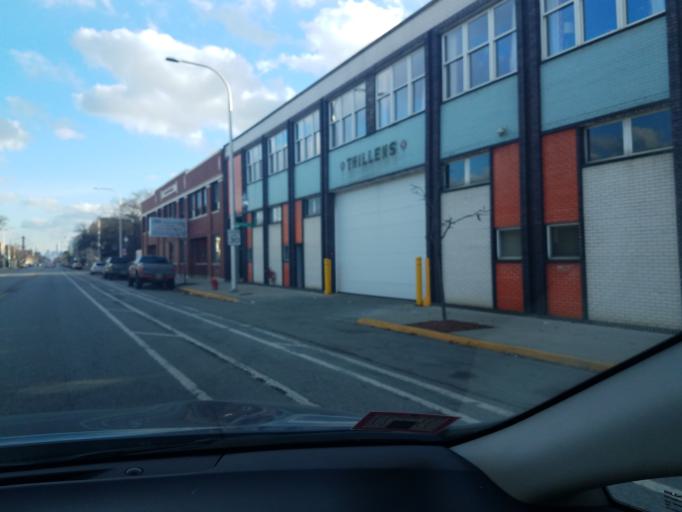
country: US
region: Illinois
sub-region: Cook County
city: Lincolnwood
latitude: 41.9582
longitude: -87.7257
